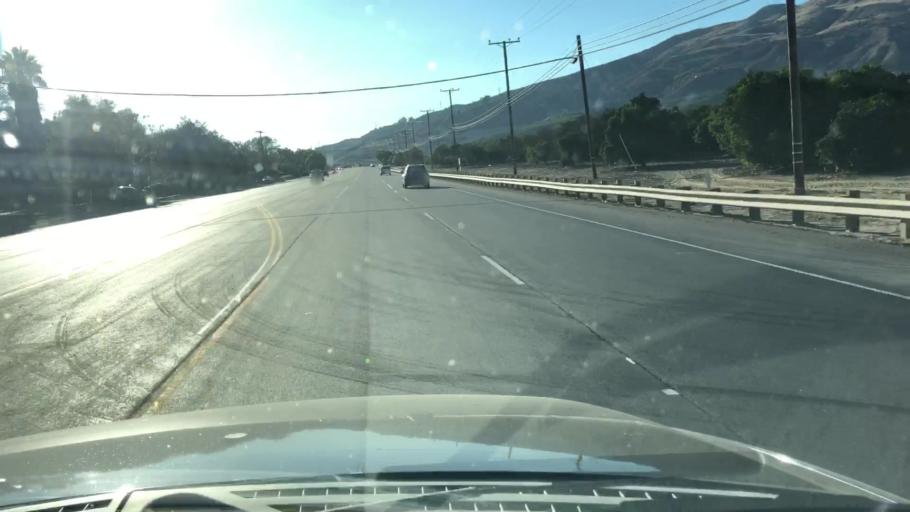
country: US
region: California
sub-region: Ventura County
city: Piru
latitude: 34.4008
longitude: -118.8214
